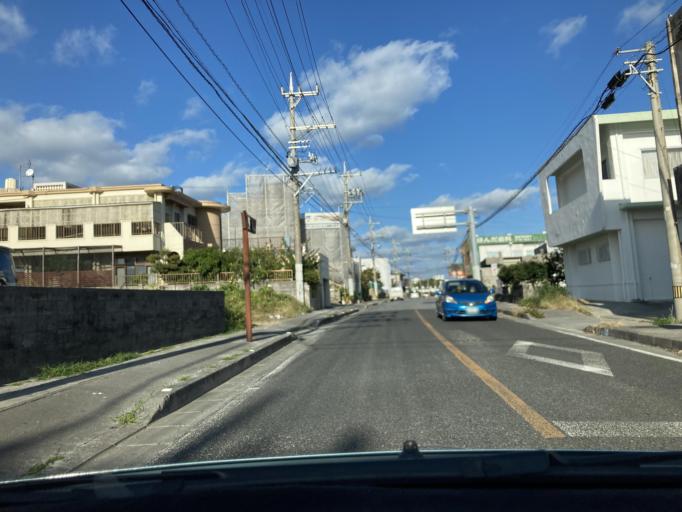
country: JP
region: Okinawa
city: Katsuren-haebaru
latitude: 26.3252
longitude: 127.8908
